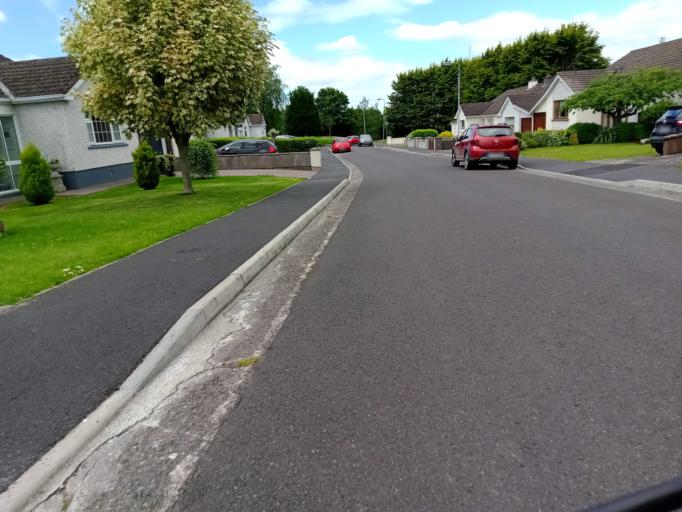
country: IE
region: Leinster
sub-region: Kilkenny
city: Kilkenny
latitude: 52.6532
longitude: -7.2390
